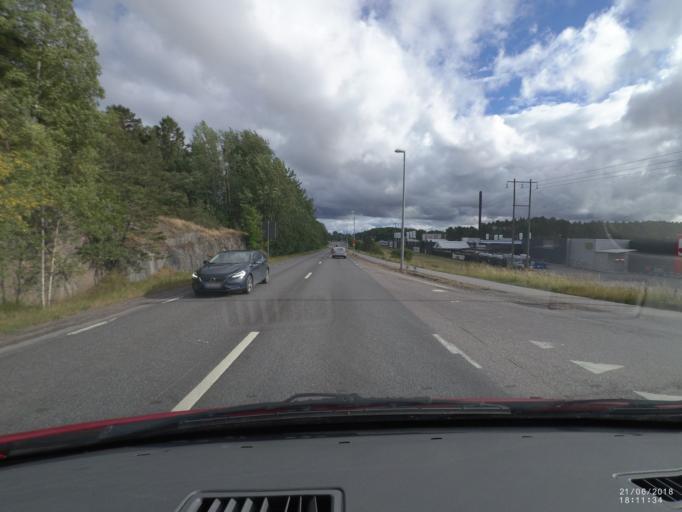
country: SE
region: Soedermanland
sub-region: Nykopings Kommun
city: Nykoping
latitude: 58.7713
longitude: 17.0272
